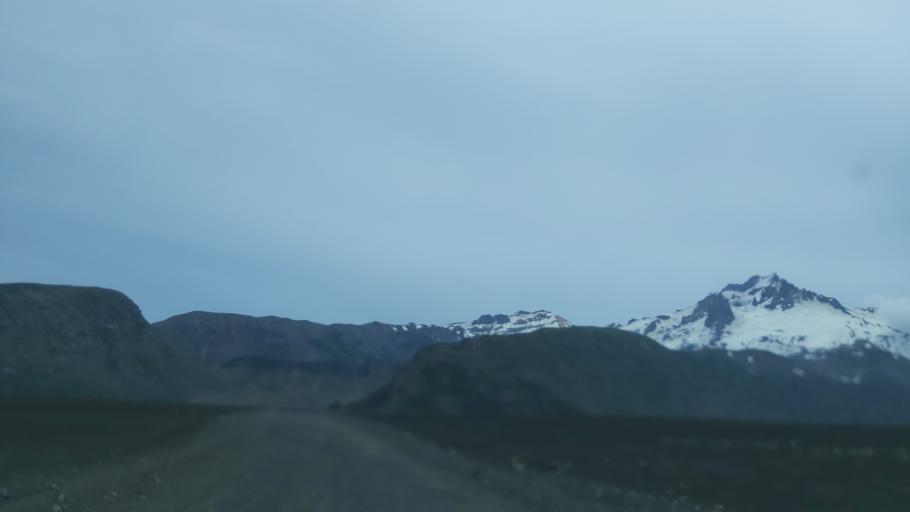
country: AR
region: Neuquen
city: Andacollo
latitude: -37.4585
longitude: -71.3031
